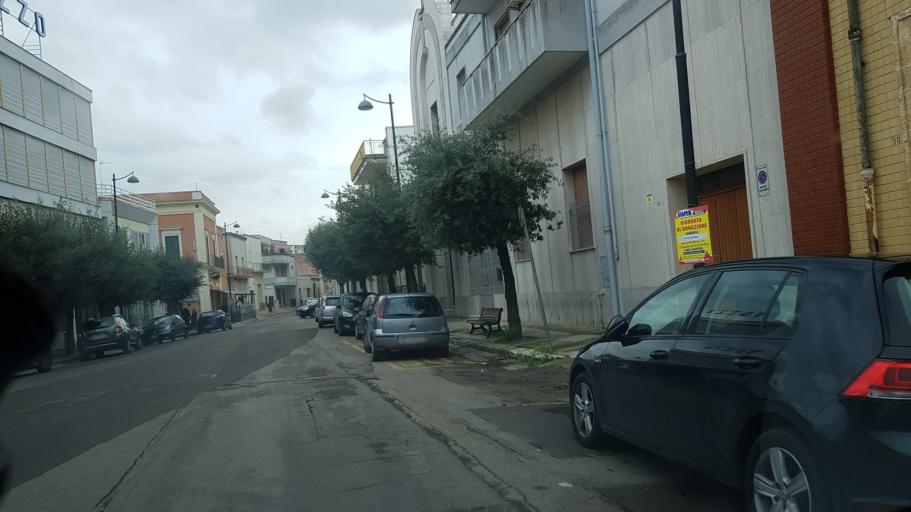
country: IT
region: Apulia
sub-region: Provincia di Lecce
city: Novoli
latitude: 40.3783
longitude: 18.0484
